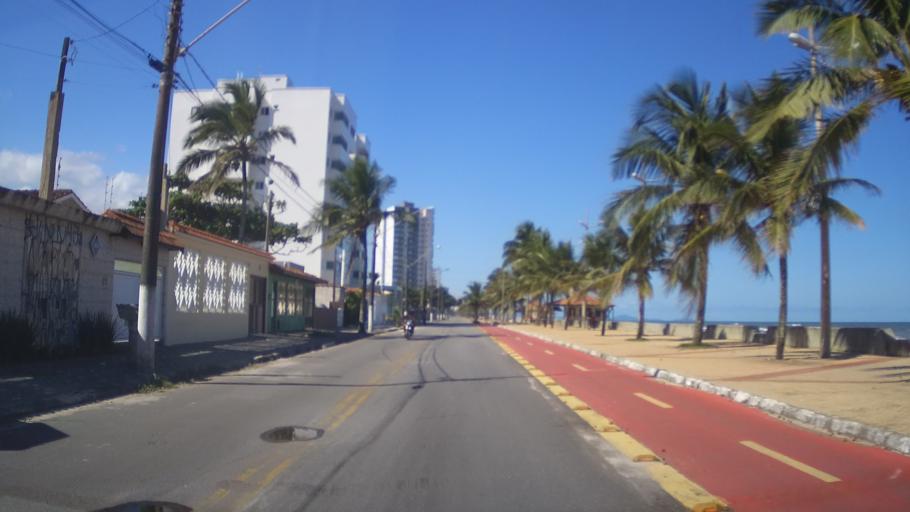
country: BR
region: Sao Paulo
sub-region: Mongagua
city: Mongagua
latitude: -24.1129
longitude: -46.6532
